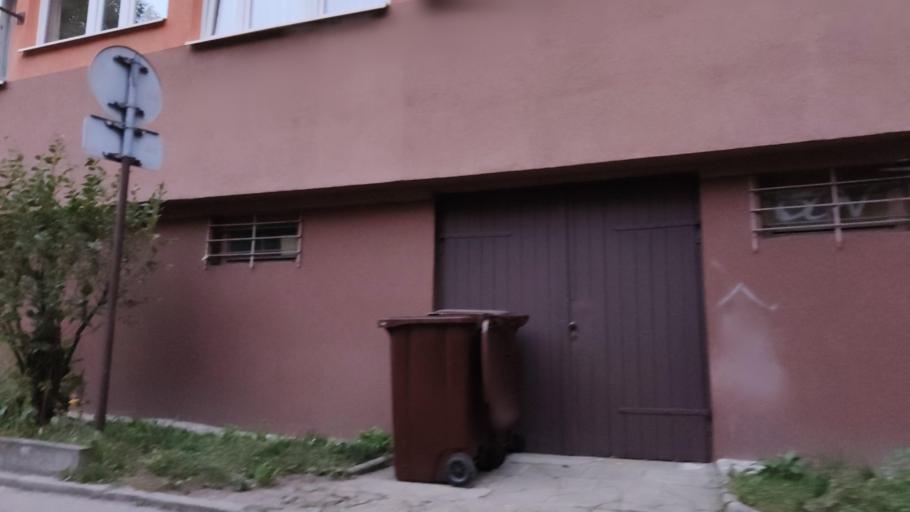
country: PL
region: Lower Silesian Voivodeship
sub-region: Powiat wroclawski
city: Wroclaw
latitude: 51.0886
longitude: 17.0228
